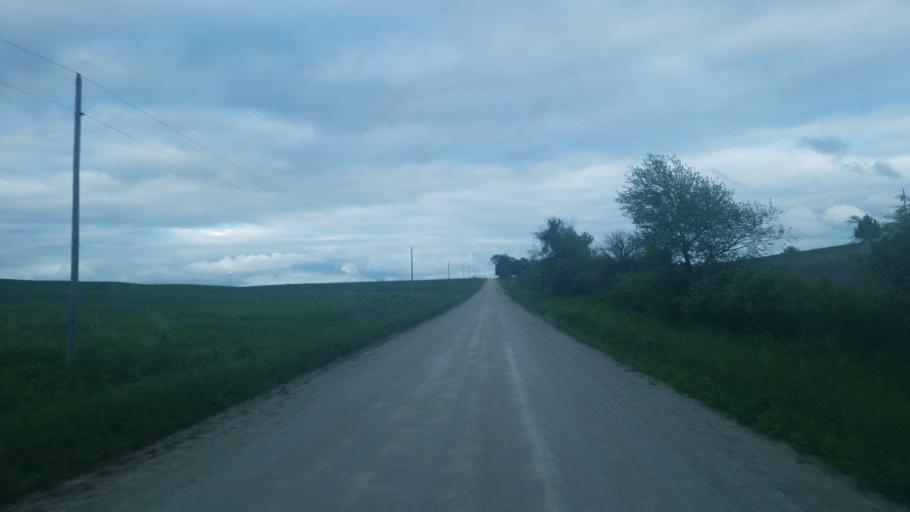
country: US
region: Iowa
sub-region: Decatur County
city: Lamoni
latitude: 40.5947
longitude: -93.9510
